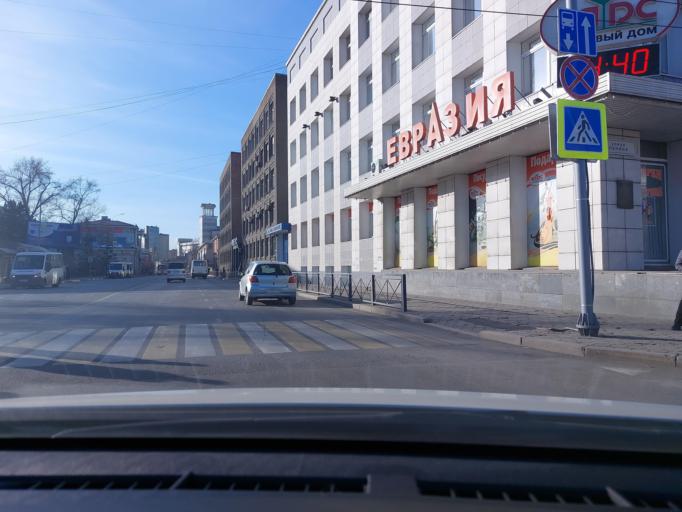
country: RU
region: Irkutsk
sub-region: Irkutskiy Rayon
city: Irkutsk
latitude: 52.2893
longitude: 104.2792
